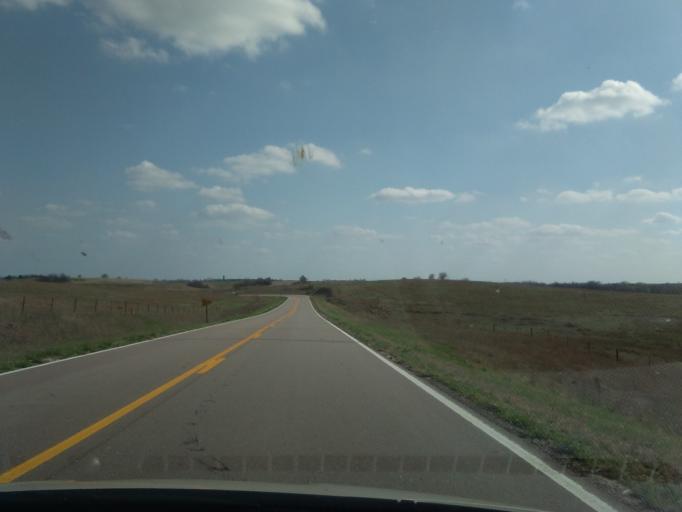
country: US
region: Nebraska
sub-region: Webster County
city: Red Cloud
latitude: 40.0062
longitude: -98.3304
